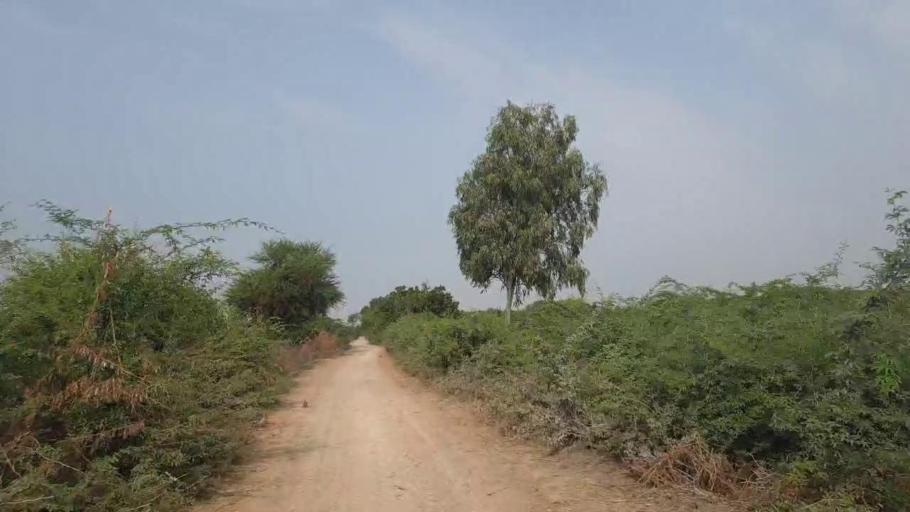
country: PK
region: Sindh
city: Badin
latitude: 24.5950
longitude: 68.7413
